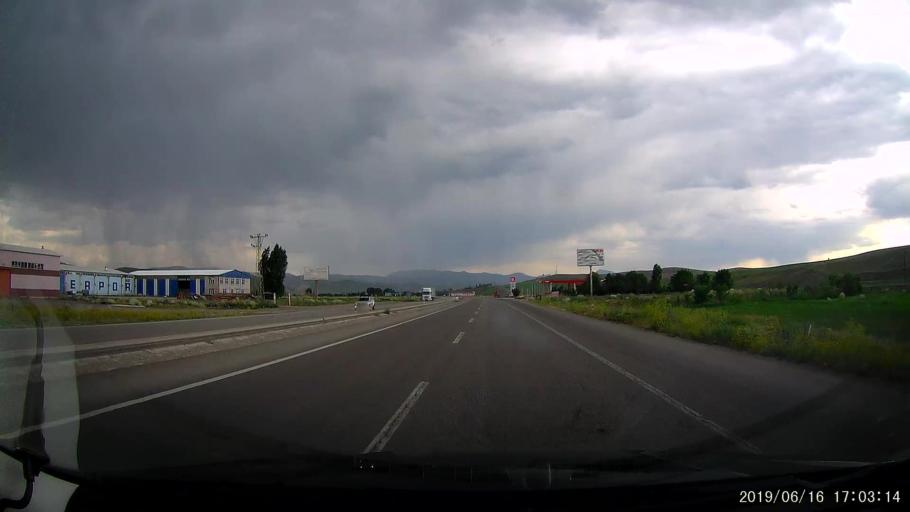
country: TR
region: Erzurum
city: Askale
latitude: 39.9383
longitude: 40.7364
